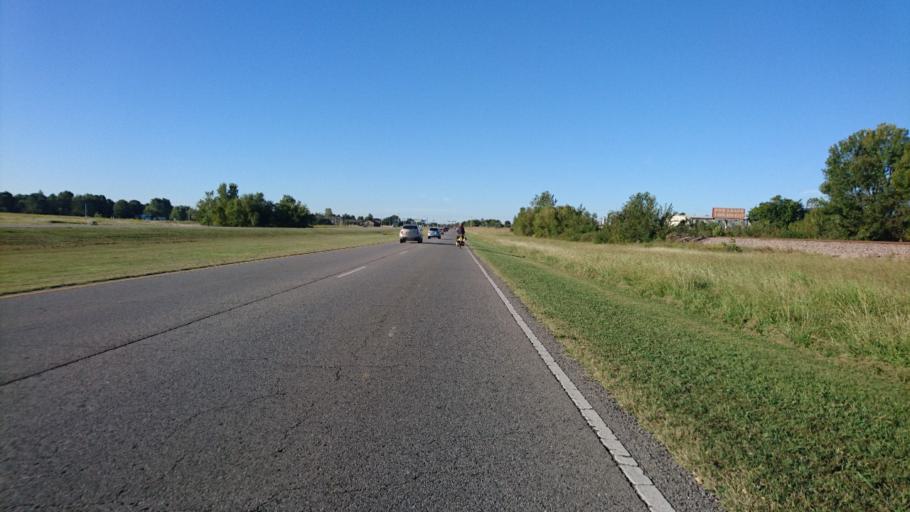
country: US
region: Oklahoma
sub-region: Rogers County
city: Claremore
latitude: 36.2831
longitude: -95.6376
